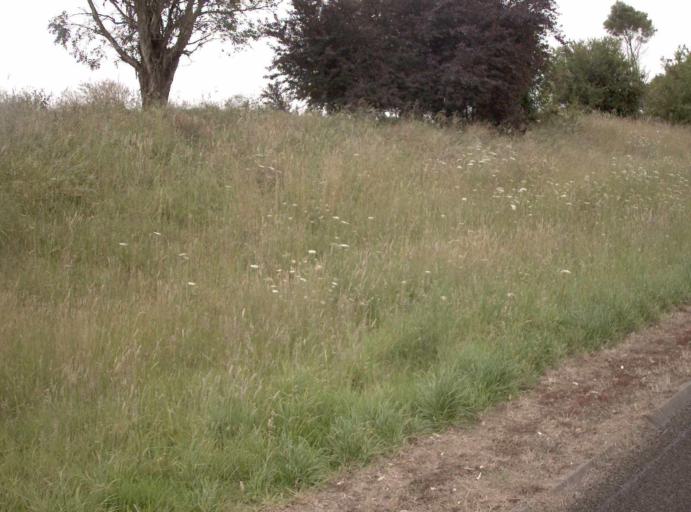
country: AU
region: Victoria
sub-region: Baw Baw
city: Warragul
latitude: -38.1518
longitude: 145.8909
